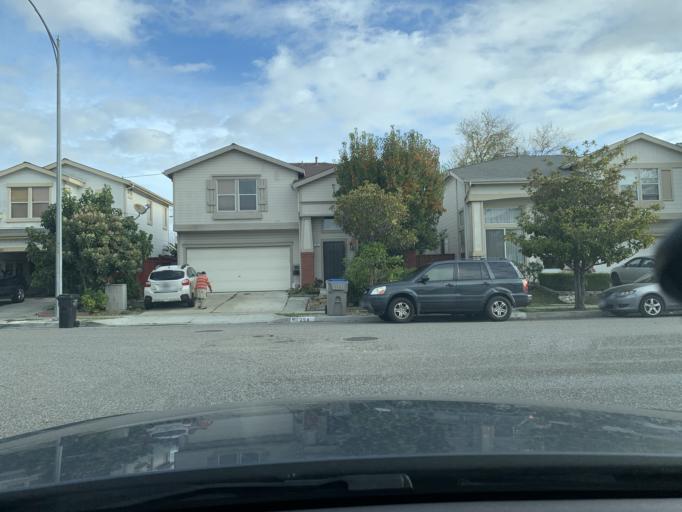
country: US
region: California
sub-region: Santa Clara County
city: Alum Rock
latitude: 37.3534
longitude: -121.8420
